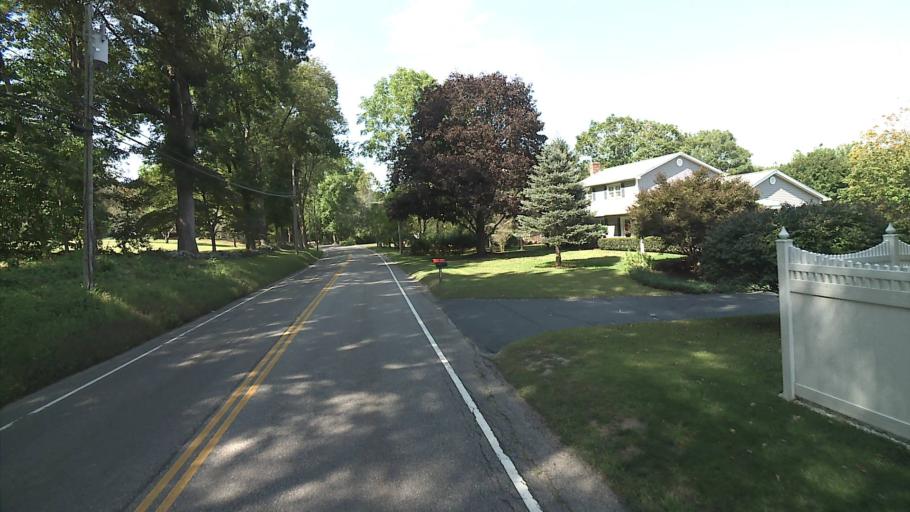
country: US
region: Connecticut
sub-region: New London County
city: Baltic
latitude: 41.5814
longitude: -72.1450
